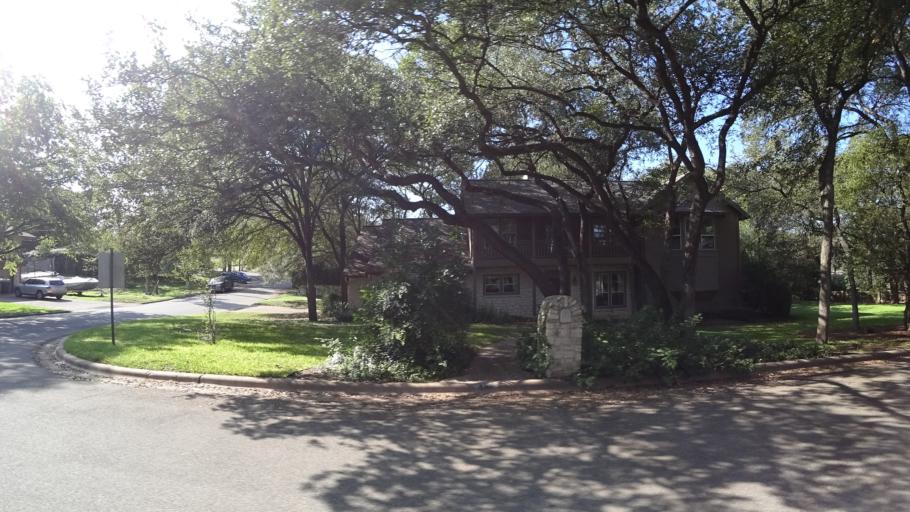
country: US
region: Texas
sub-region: Travis County
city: Rollingwood
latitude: 30.2798
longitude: -97.7987
